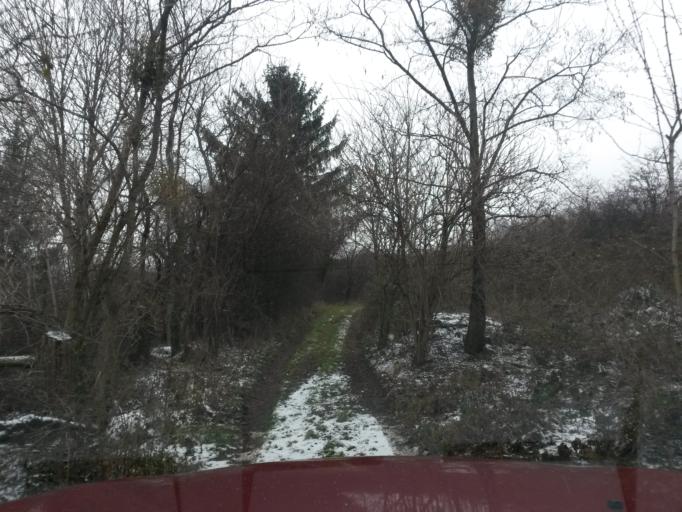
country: SK
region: Kosicky
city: Kosice
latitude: 48.7203
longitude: 21.2832
